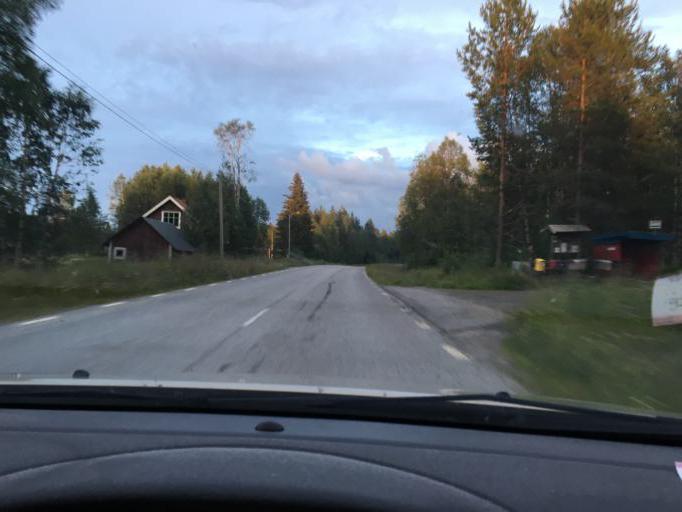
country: SE
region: Norrbotten
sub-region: Lulea Kommun
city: Ranea
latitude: 66.0457
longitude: 22.2848
